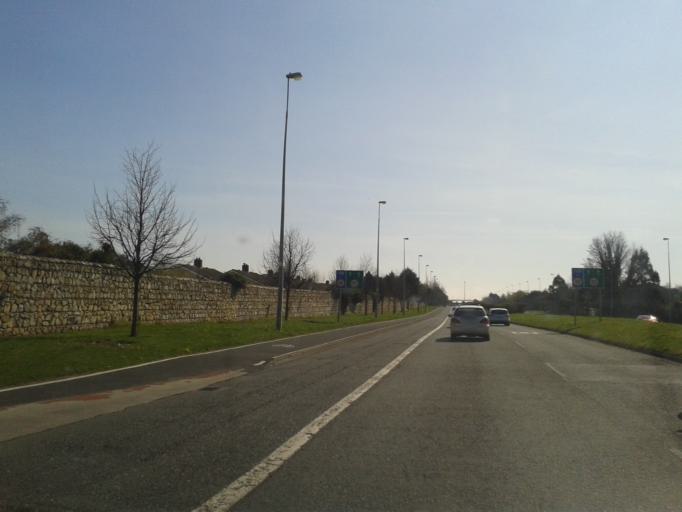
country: IE
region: Leinster
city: Cabinteely
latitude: 53.2659
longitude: -6.1578
